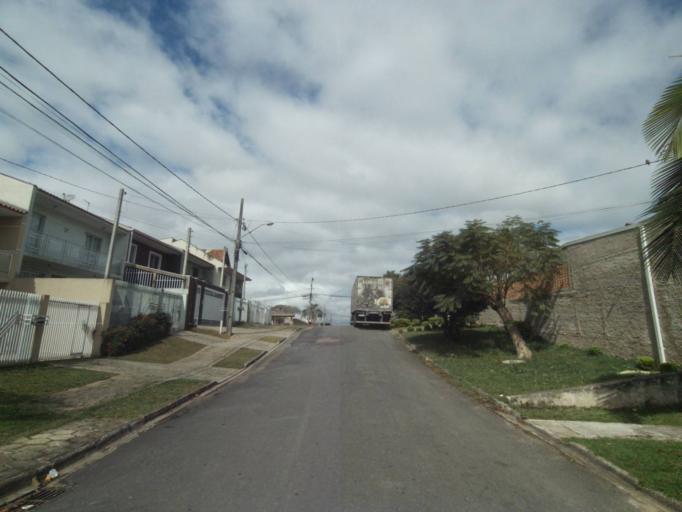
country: BR
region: Parana
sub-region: Sao Jose Dos Pinhais
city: Sao Jose dos Pinhais
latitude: -25.5368
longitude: -49.2910
